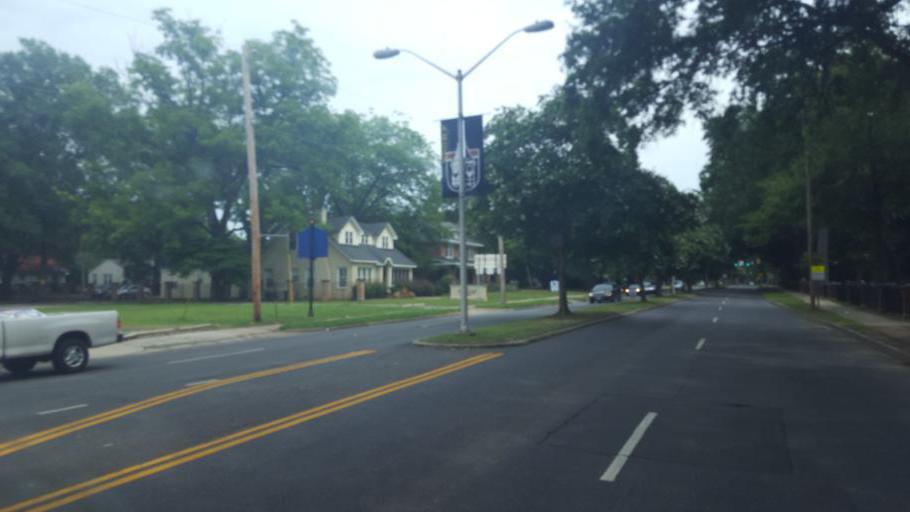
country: US
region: South Carolina
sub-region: York County
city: Rock Hill
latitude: 34.9428
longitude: -81.0310
